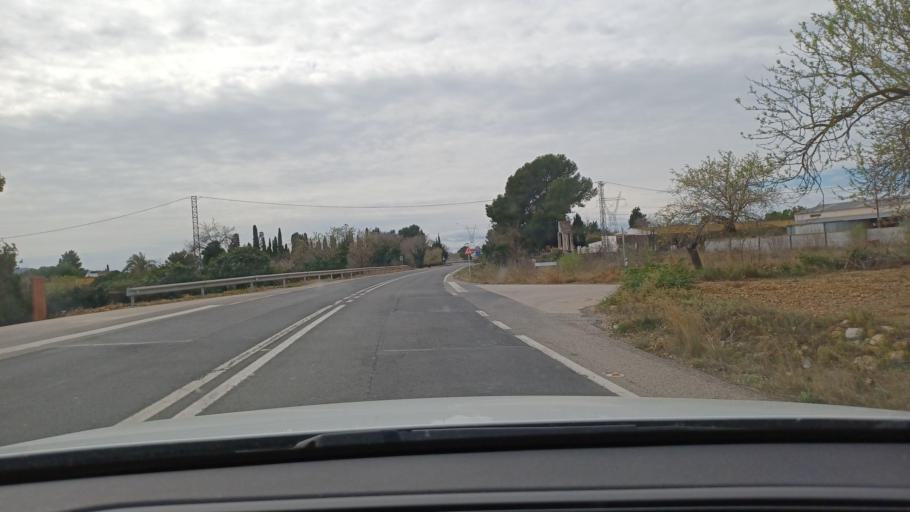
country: ES
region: Catalonia
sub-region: Provincia de Tarragona
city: Santa Barbara
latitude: 40.6833
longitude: 0.4616
